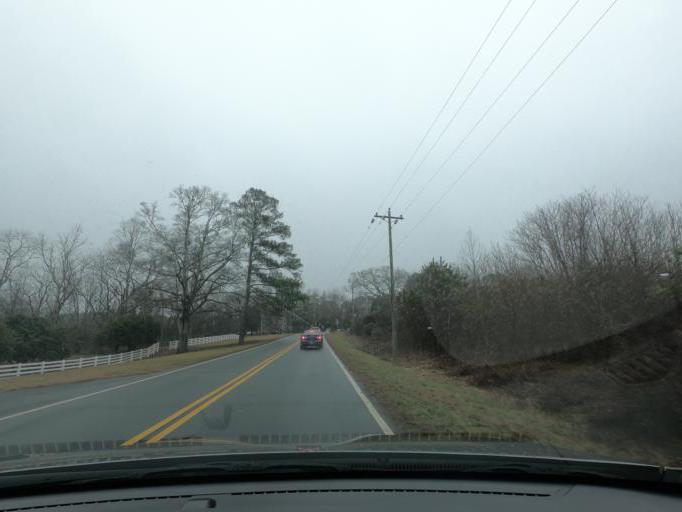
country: US
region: Georgia
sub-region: Fulton County
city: Milton
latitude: 34.1141
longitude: -84.3153
